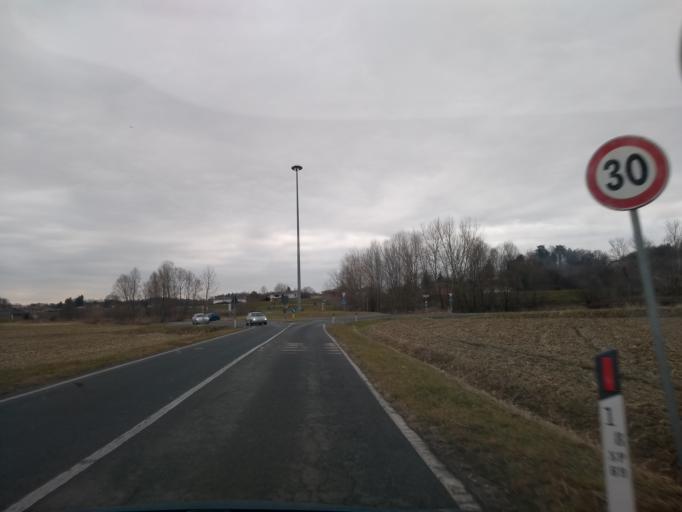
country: IT
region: Piedmont
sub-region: Provincia di Torino
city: Salerano Canavese
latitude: 45.4638
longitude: 7.8462
